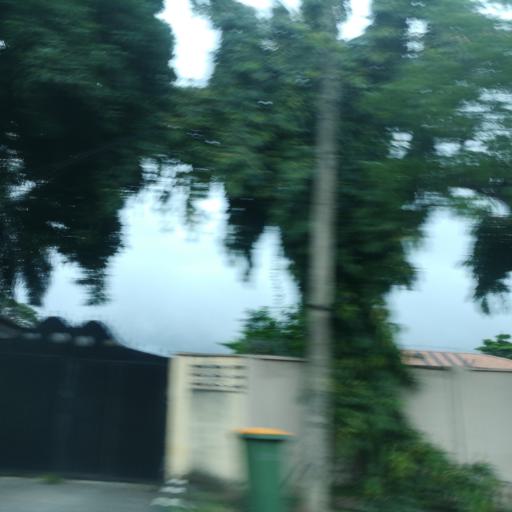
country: NG
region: Lagos
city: Ikoyi
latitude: 6.4547
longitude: 3.4468
